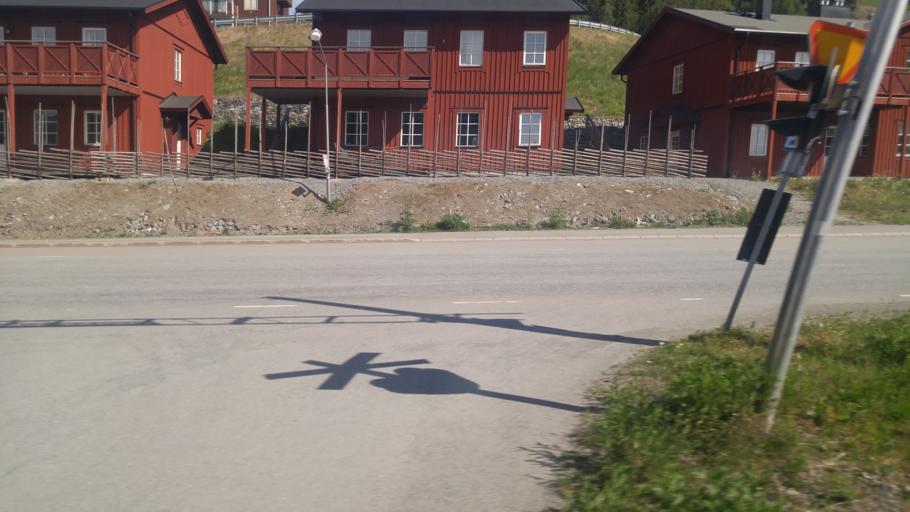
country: SE
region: Jaemtland
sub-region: Are Kommun
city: Are
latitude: 63.4031
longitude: 13.0527
